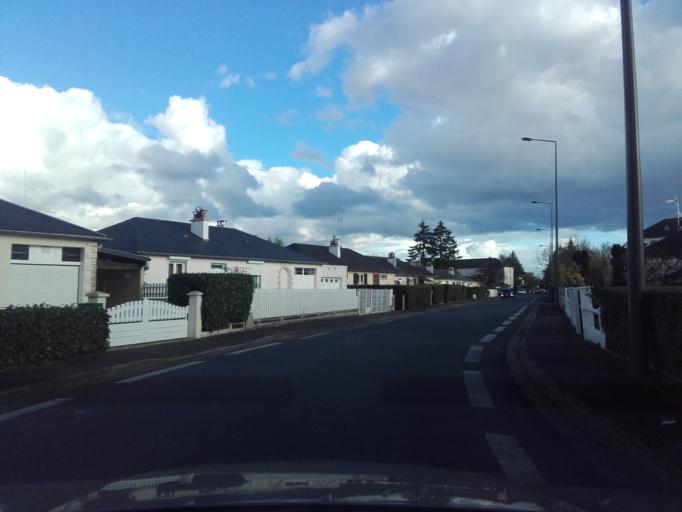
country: FR
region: Centre
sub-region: Departement d'Indre-et-Loire
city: Saint-Cyr-sur-Loire
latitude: 47.4275
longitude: 0.6757
